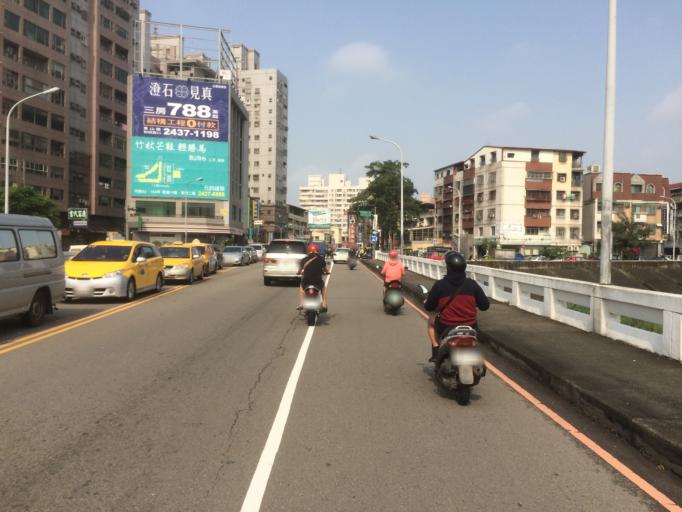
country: TW
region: Taiwan
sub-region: Taichung City
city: Taichung
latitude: 24.1695
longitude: 120.7056
